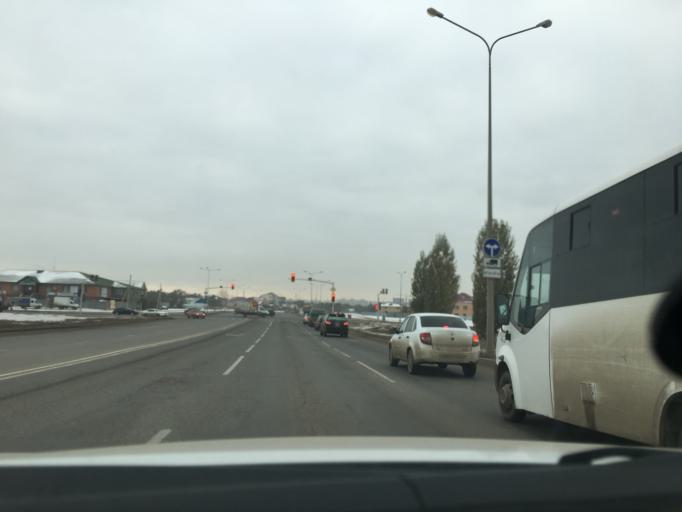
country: KZ
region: Astana Qalasy
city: Astana
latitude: 51.1382
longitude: 71.5224
